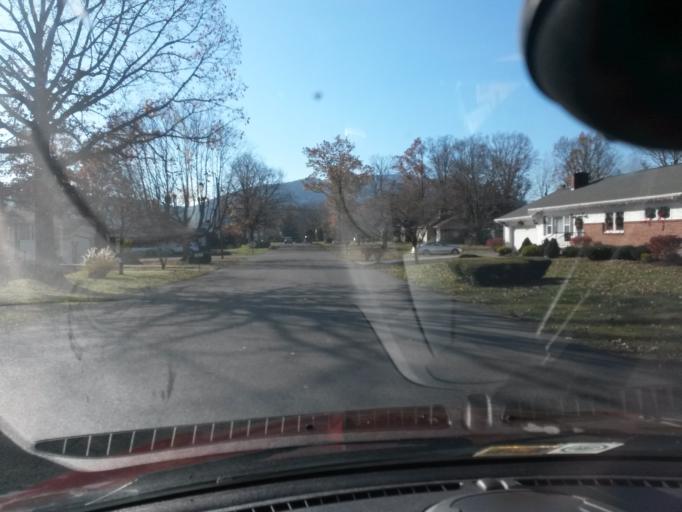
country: US
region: Virginia
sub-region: Alleghany County
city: Clifton Forge
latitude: 37.8273
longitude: -79.8231
